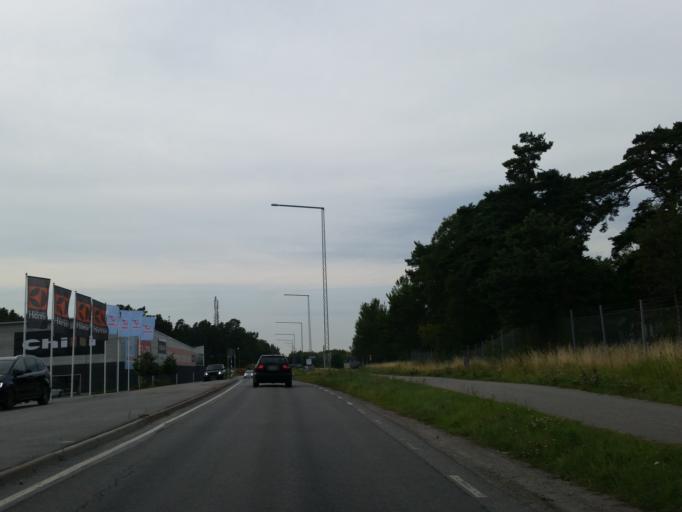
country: SE
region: Stockholm
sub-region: Jarfalla Kommun
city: Jakobsberg
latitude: 59.4143
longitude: 17.8574
